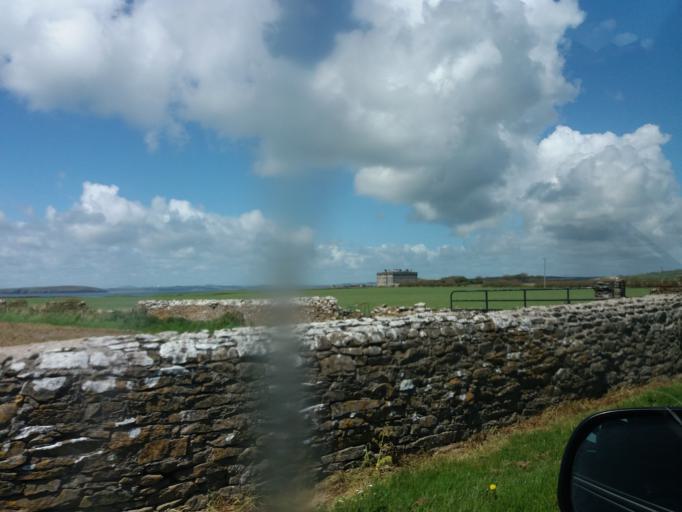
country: IE
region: Munster
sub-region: Waterford
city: Dunmore East
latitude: 52.1439
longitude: -6.9098
